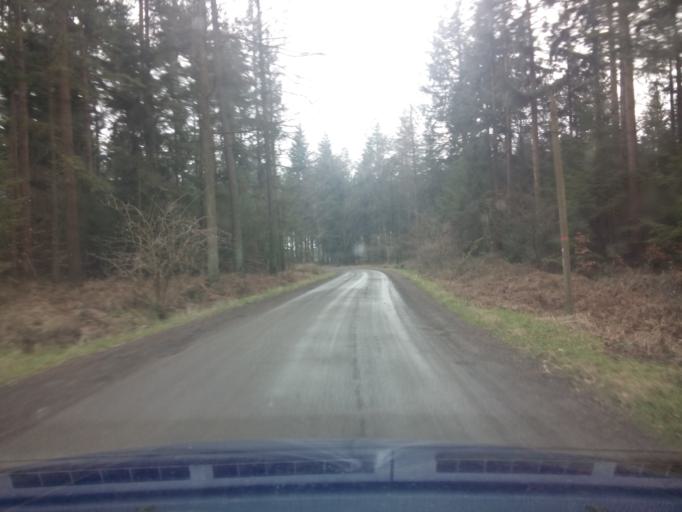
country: DE
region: Lower Saxony
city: Drangstedt
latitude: 53.6154
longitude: 8.7269
